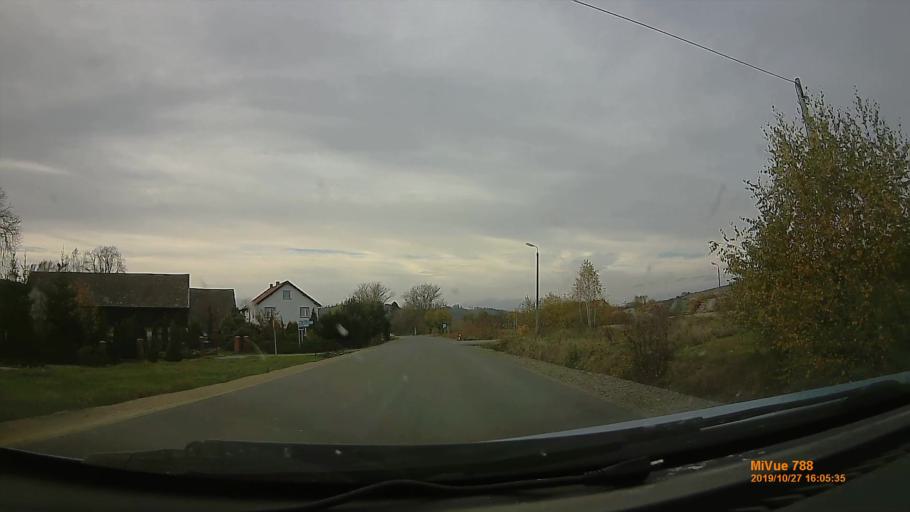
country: PL
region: Lower Silesian Voivodeship
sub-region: Powiat klodzki
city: Nowa Ruda
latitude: 50.5323
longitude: 16.4819
